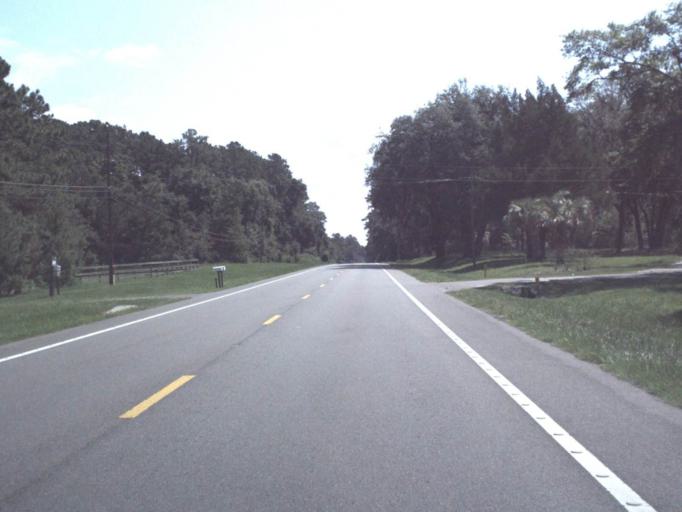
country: US
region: Florida
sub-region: Alachua County
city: Gainesville
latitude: 29.6631
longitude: -82.2528
